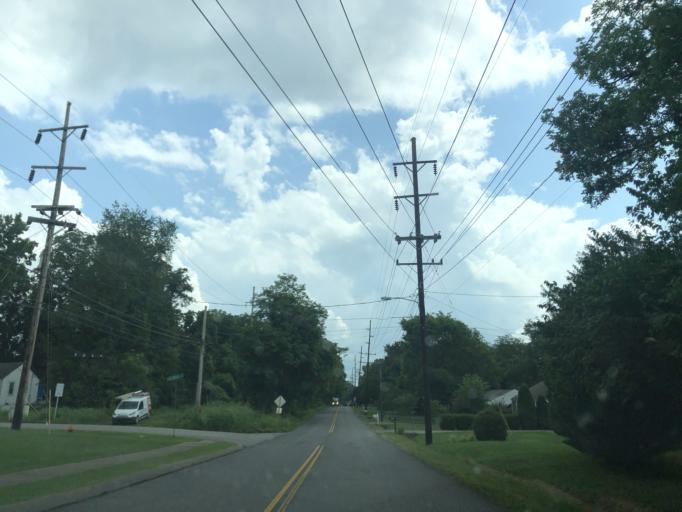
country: US
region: Tennessee
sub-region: Davidson County
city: Lakewood
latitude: 36.1617
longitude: -86.6582
